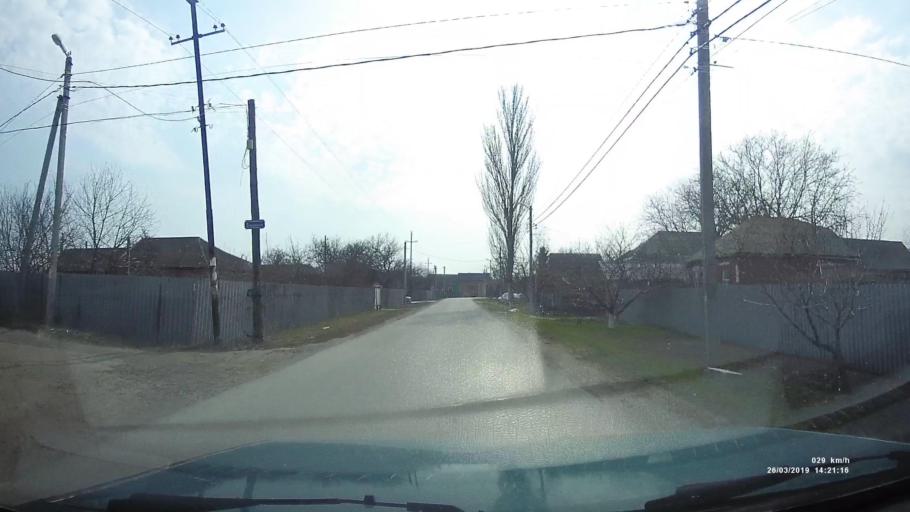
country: RU
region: Rostov
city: Novobessergenovka
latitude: 47.1867
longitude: 38.8691
